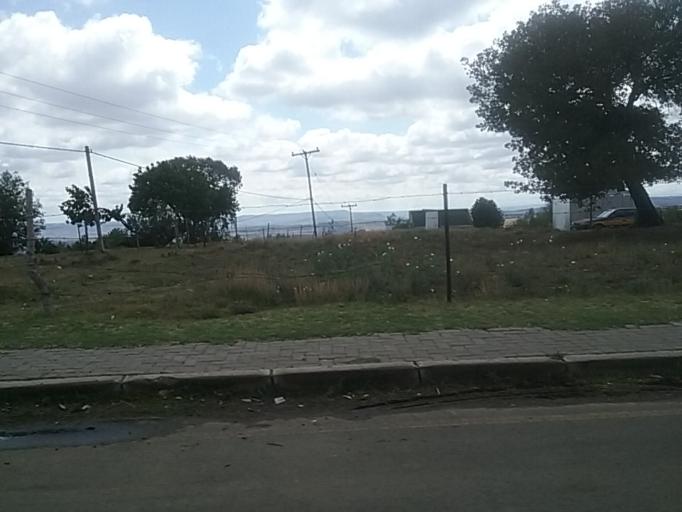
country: LS
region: Berea
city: Teyateyaneng
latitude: -29.1391
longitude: 27.7356
